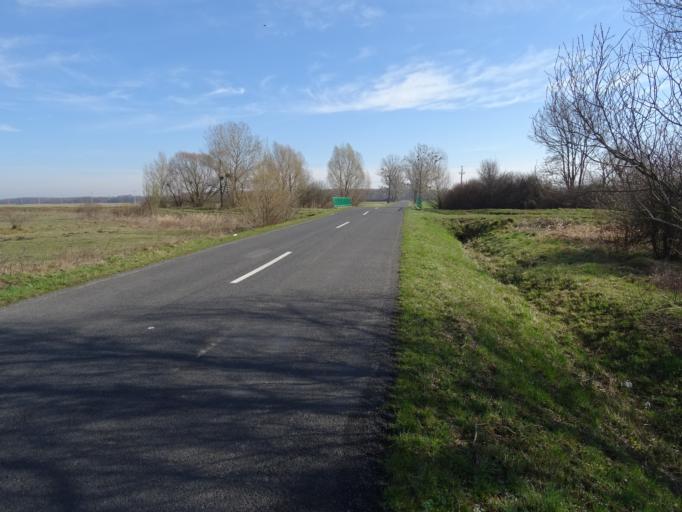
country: HU
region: Gyor-Moson-Sopron
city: Kapuvar
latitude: 47.5235
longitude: 17.0229
